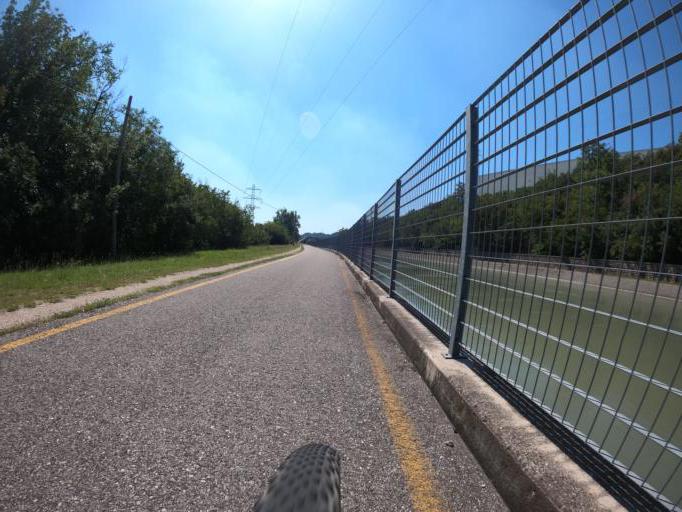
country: IT
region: Veneto
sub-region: Provincia di Verona
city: Volargne
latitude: 45.5339
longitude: 10.8040
